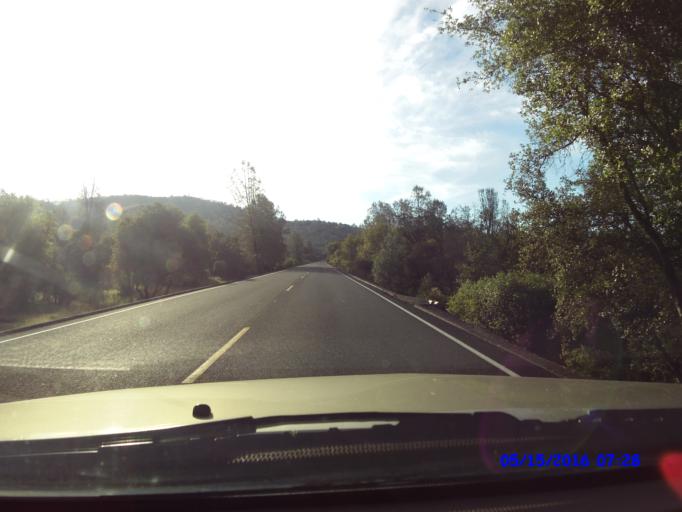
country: US
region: California
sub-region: Tuolumne County
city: Tuolumne City
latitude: 37.7342
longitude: -120.2219
